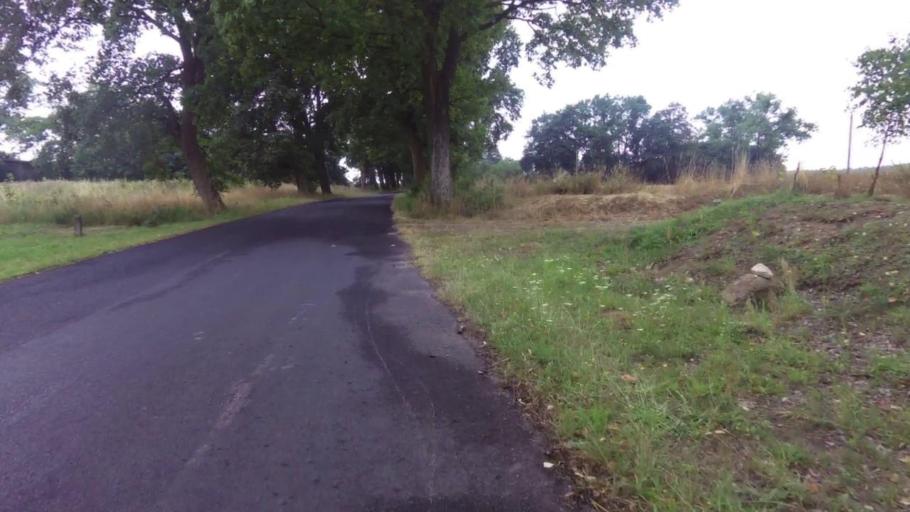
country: PL
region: West Pomeranian Voivodeship
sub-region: Powiat choszczenski
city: Choszczno
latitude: 53.2160
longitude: 15.3900
